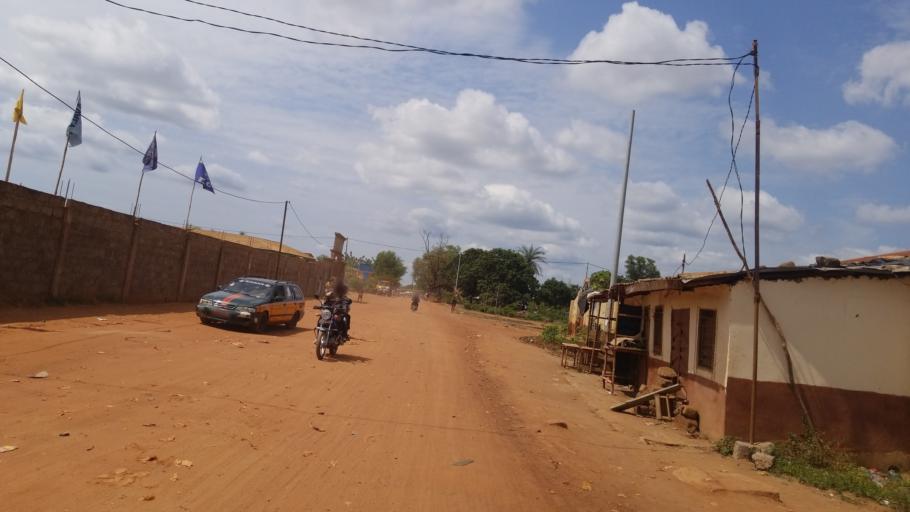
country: SL
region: Western Area
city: Waterloo
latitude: 8.3245
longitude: -13.0643
